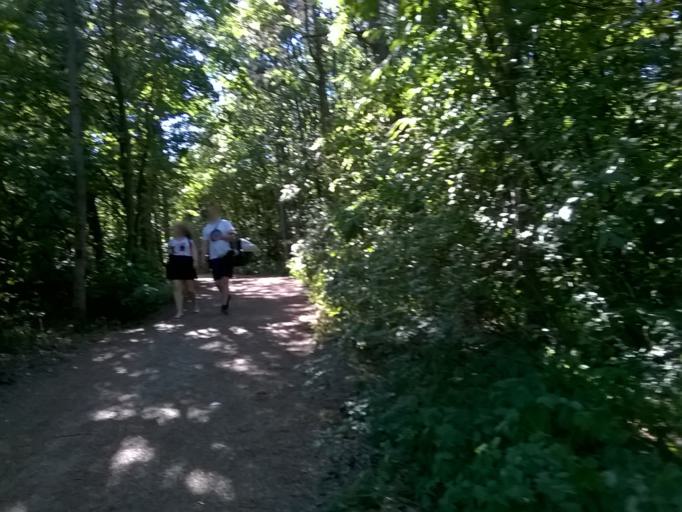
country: SK
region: Nitriansky
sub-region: Okres Nitra
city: Nitra
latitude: 48.3571
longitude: 18.0584
